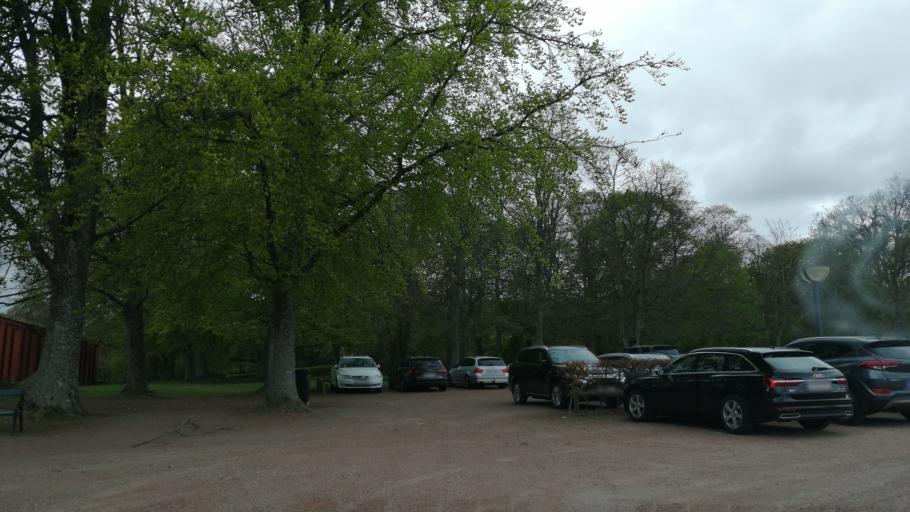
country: SE
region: Skane
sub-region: Kristianstads Kommun
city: Fjalkinge
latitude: 56.0859
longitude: 14.3488
